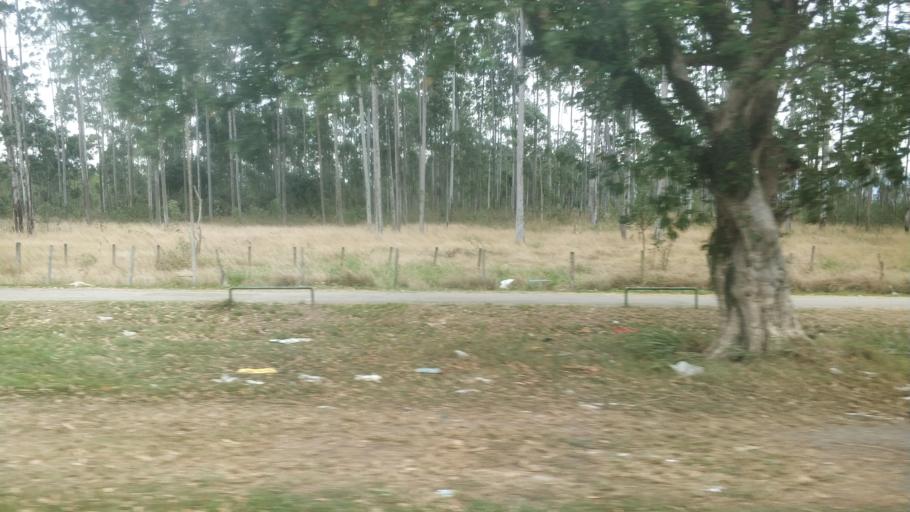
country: BR
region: Rio de Janeiro
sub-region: Seropedica
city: Seropedica
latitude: -22.7883
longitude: -43.6537
